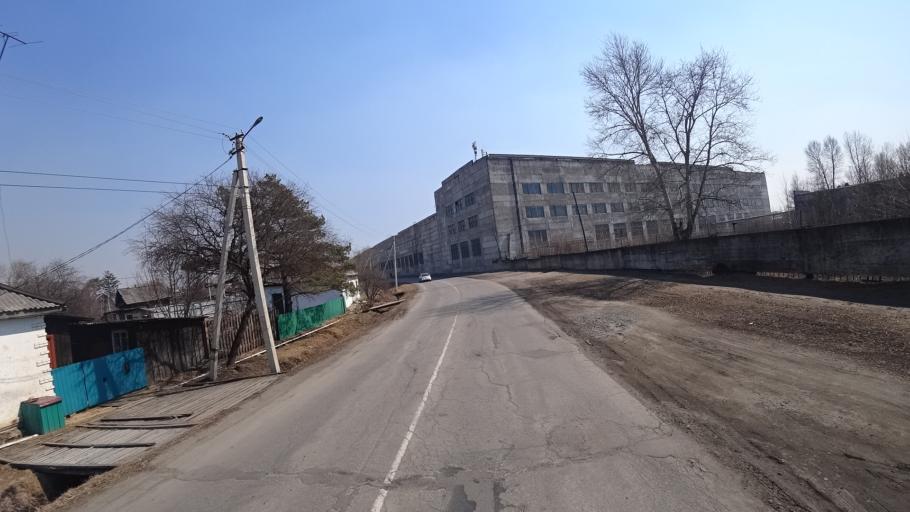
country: RU
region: Amur
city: Novobureyskiy
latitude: 49.7926
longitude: 129.8572
